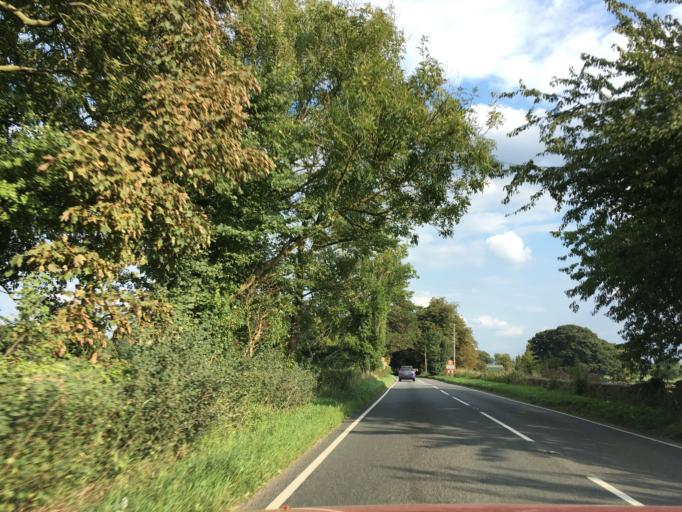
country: GB
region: England
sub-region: Gloucestershire
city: Tetbury
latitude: 51.6448
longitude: -2.2071
